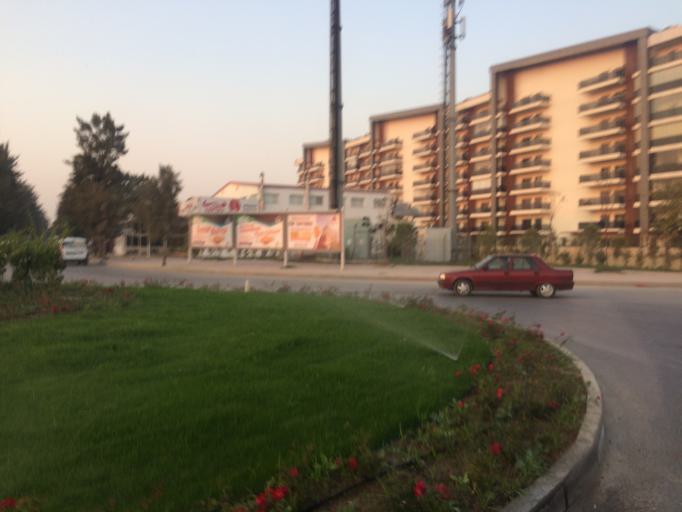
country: TR
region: Izmir
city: Karsiyaka
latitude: 38.4936
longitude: 27.0466
